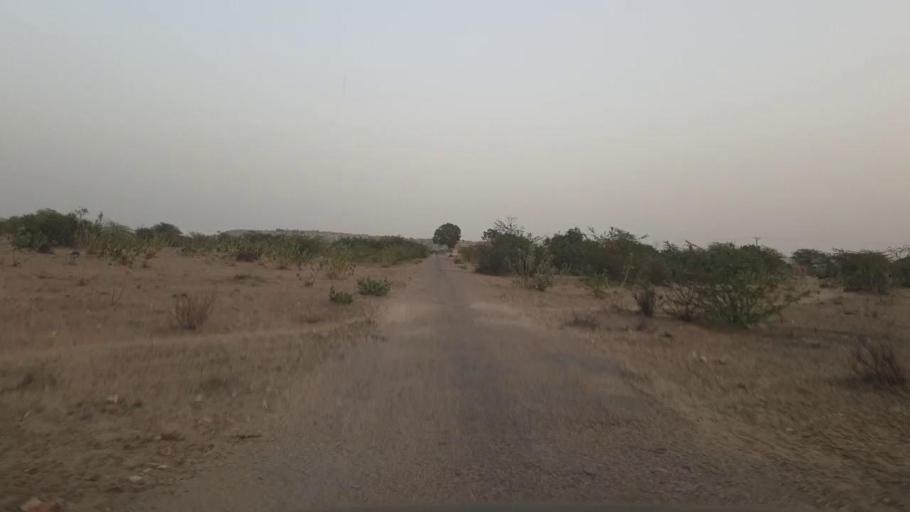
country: PK
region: Sindh
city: Chor
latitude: 25.5009
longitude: 69.8225
